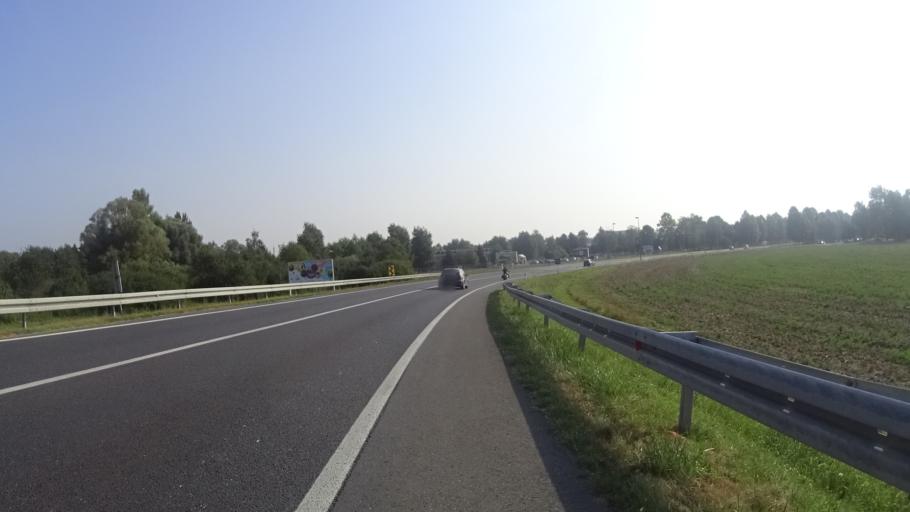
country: HR
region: Medimurska
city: Strahoninec
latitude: 46.3868
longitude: 16.4057
